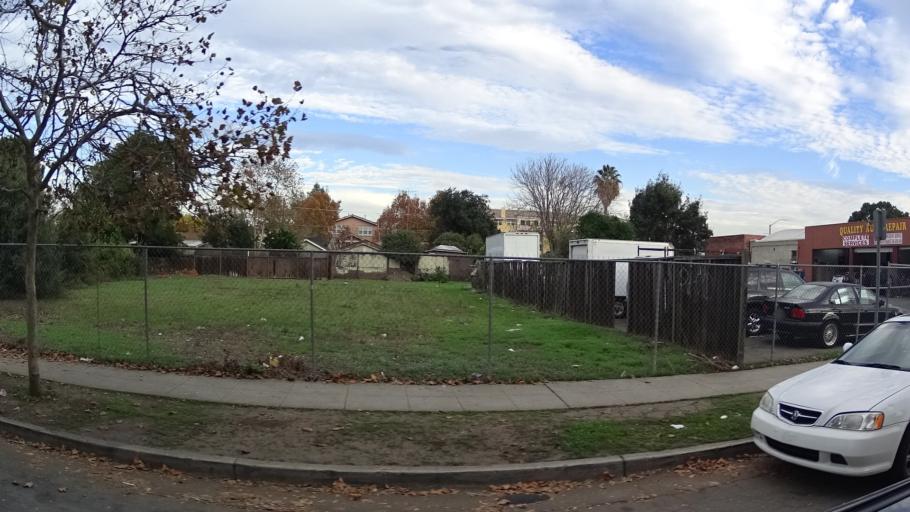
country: US
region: California
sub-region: Santa Clara County
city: Buena Vista
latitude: 37.3241
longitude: -121.9200
